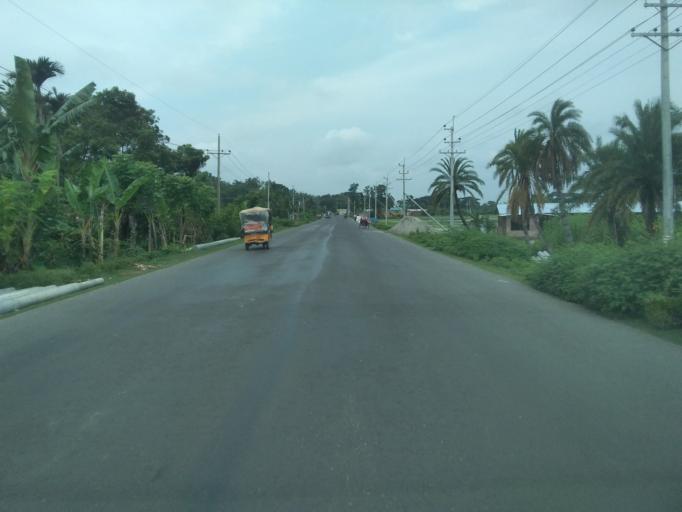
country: BD
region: Khulna
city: Satkhira
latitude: 22.7674
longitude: 89.1457
